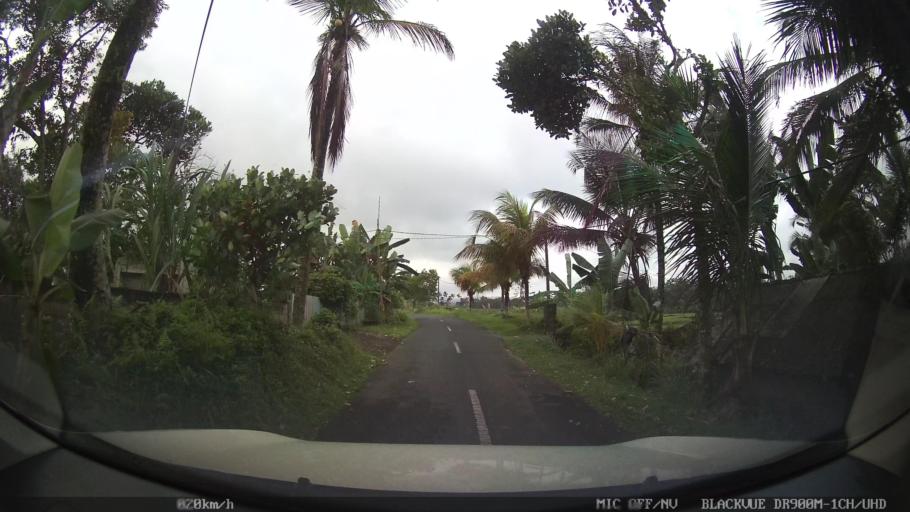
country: ID
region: Bali
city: Badung
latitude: -8.4226
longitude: 115.2273
